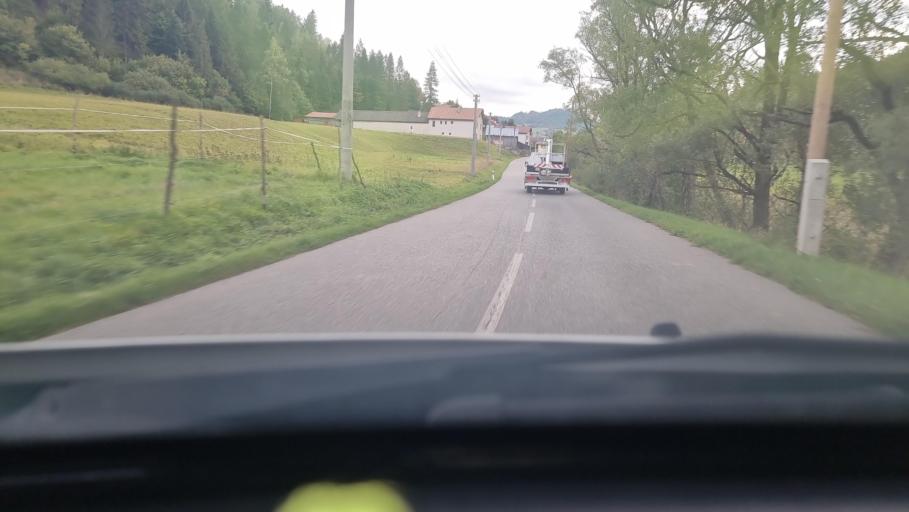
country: PL
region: Lesser Poland Voivodeship
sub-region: Powiat nowotarski
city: Szczawnica
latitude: 49.3518
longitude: 20.4426
